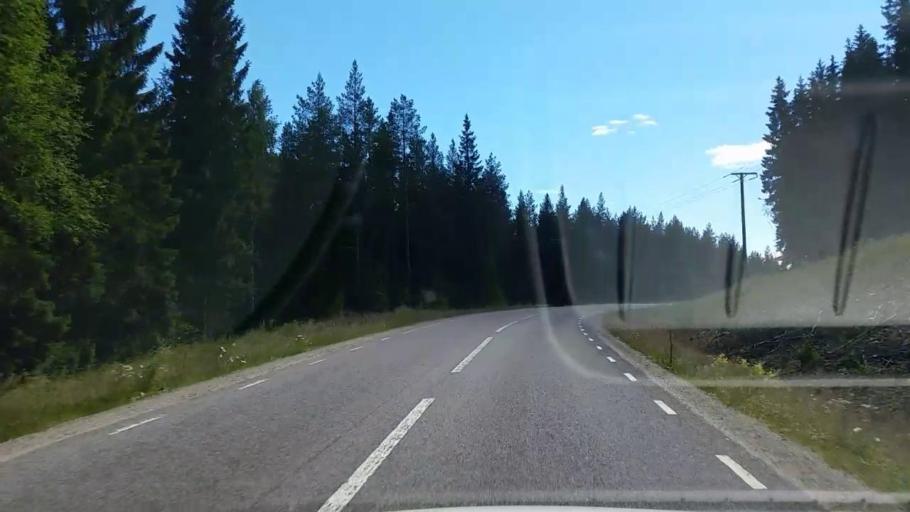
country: SE
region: Gaevleborg
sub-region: Ovanakers Kommun
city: Edsbyn
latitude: 61.5275
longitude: 15.6799
